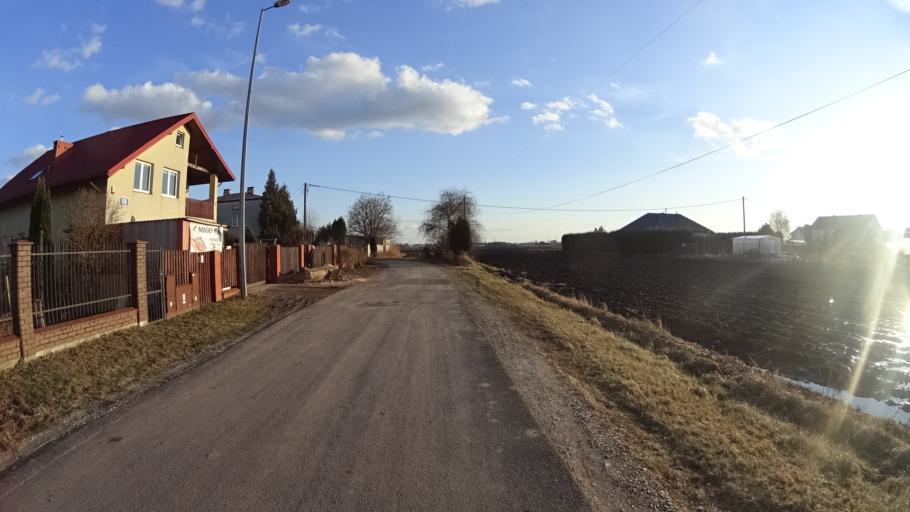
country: PL
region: Masovian Voivodeship
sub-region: Powiat warszawski zachodni
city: Truskaw
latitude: 52.2531
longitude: 20.7568
